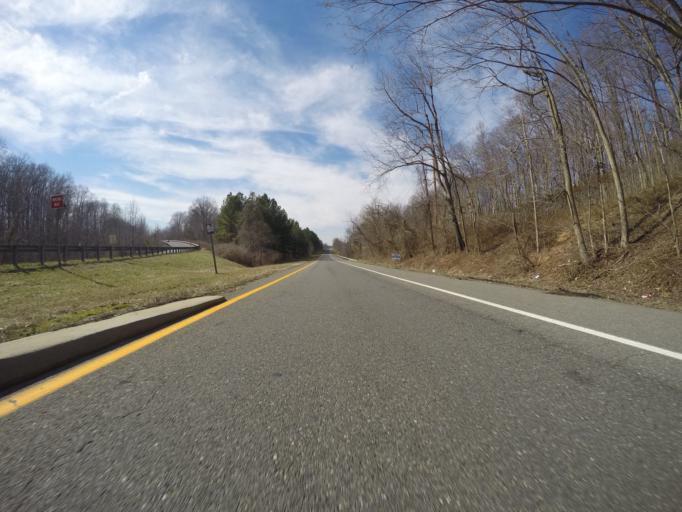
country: US
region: Maryland
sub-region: Anne Arundel County
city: Crownsville
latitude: 39.0429
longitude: -76.6105
